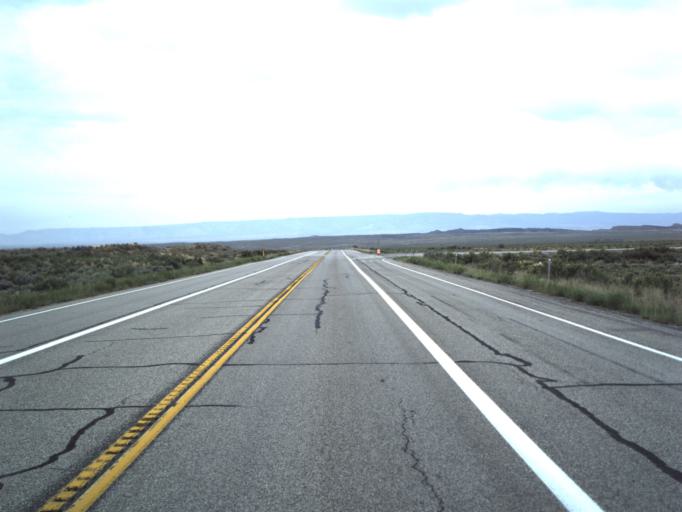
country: US
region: Utah
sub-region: Carbon County
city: East Carbon City
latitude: 39.5342
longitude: -110.5213
